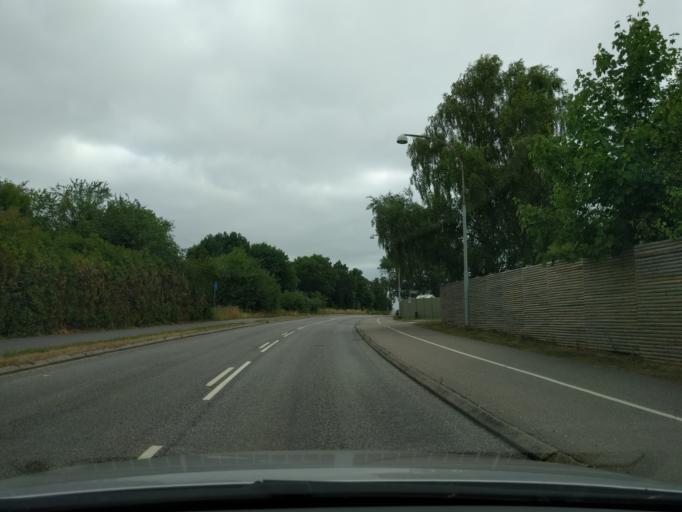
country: DK
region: Capital Region
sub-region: Helsingor Kommune
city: Espergaerde
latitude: 56.0039
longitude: 12.5411
